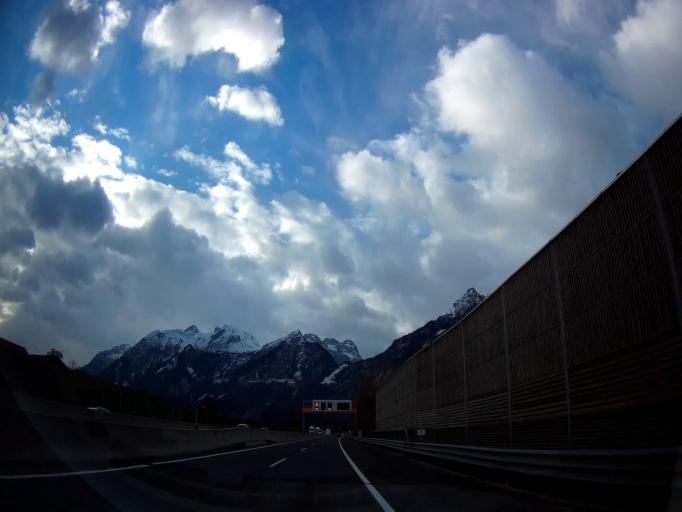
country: AT
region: Salzburg
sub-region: Politischer Bezirk Hallein
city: Golling an der Salzach
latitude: 47.6055
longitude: 13.1477
